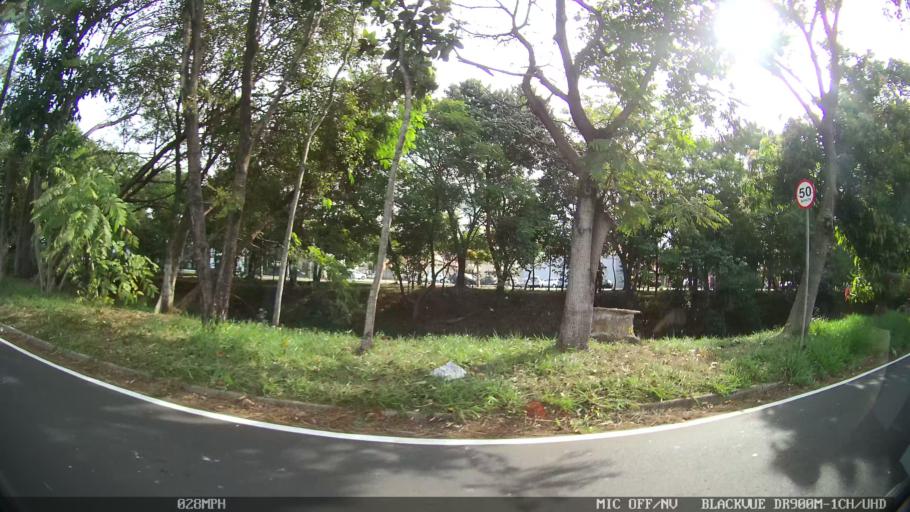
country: BR
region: Sao Paulo
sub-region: Piracicaba
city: Piracicaba
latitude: -22.7219
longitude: -47.6246
